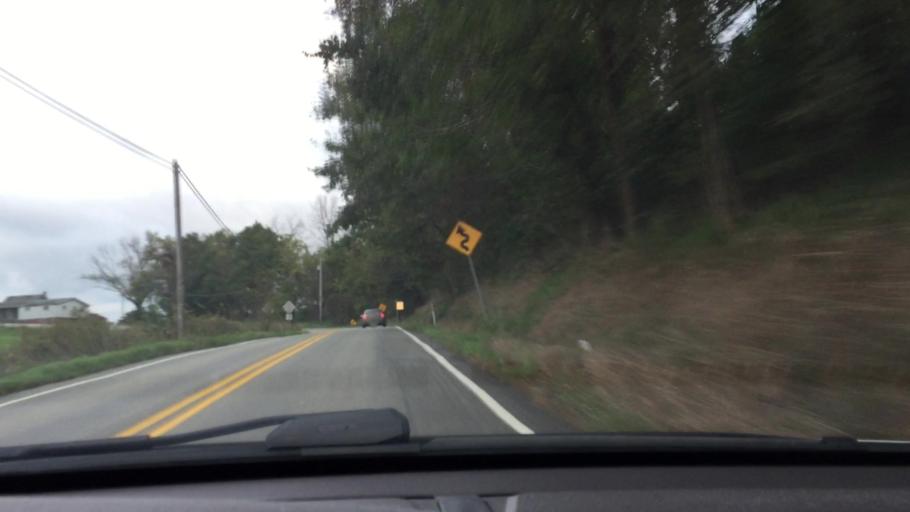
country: US
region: Pennsylvania
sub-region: Washington County
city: McMurray
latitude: 40.1895
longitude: -80.1042
